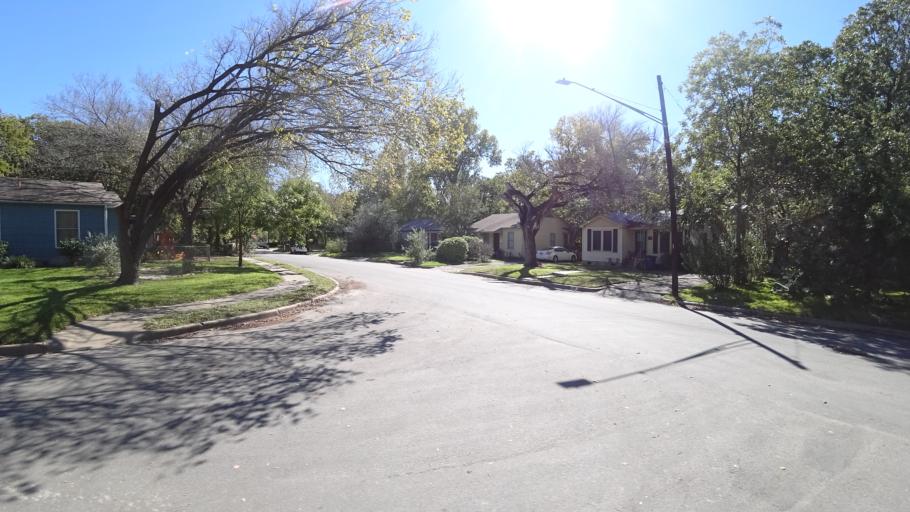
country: US
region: Texas
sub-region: Travis County
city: Austin
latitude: 30.2848
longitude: -97.7074
